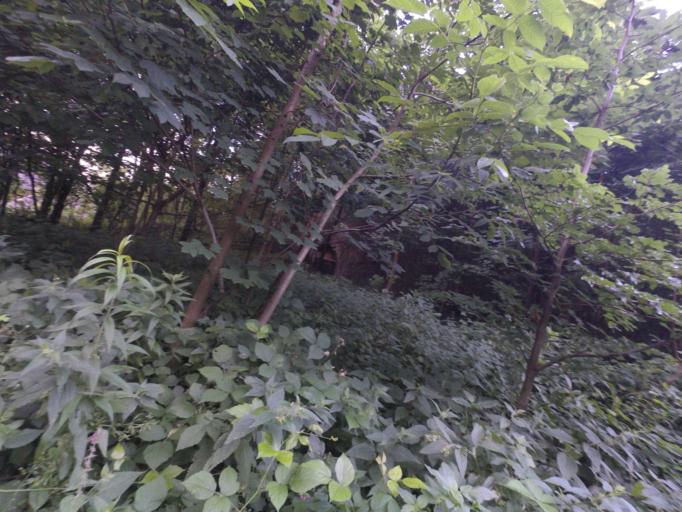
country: AT
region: Salzburg
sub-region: Politischer Bezirk Salzburg-Umgebung
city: Anif
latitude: 47.7666
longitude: 13.0550
